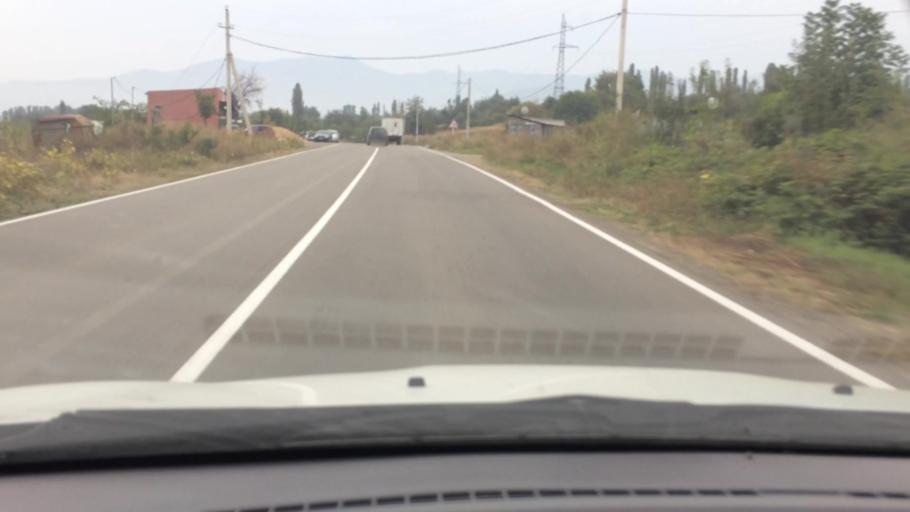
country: AM
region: Tavush
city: Bagratashen
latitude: 41.2684
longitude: 44.7911
